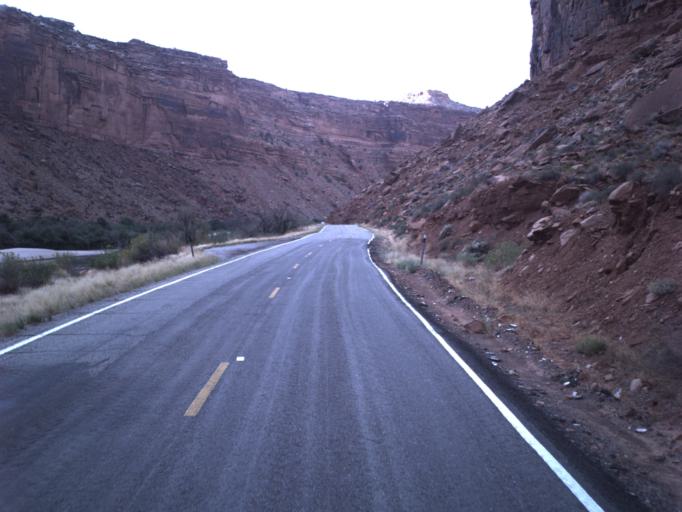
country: US
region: Utah
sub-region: Grand County
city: Moab
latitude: 38.7910
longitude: -109.3355
